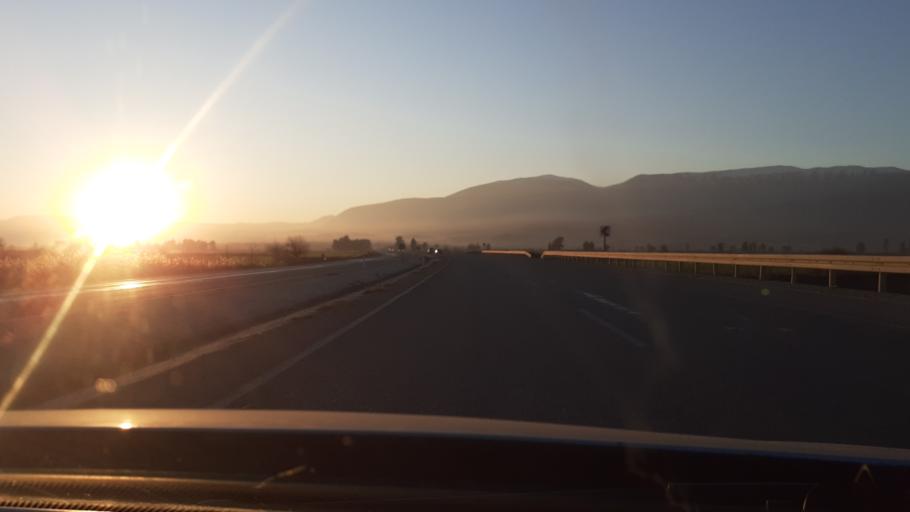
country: TR
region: Hatay
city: Kirikhan
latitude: 36.5069
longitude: 36.4312
